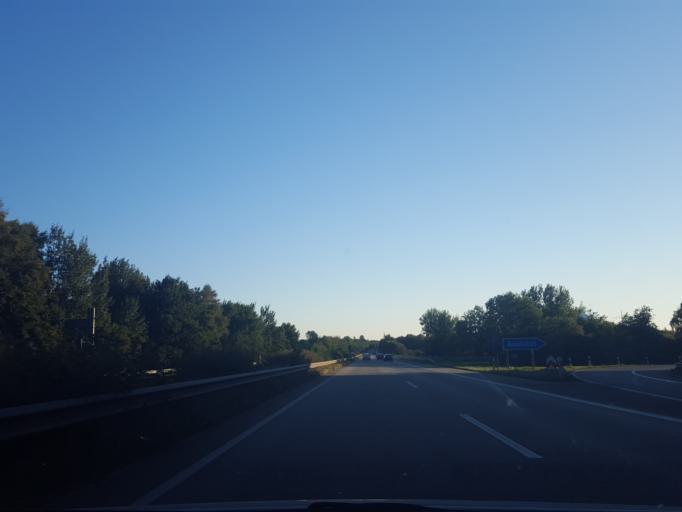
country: DE
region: Lower Saxony
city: Loxstedt
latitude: 53.4956
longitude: 8.6263
